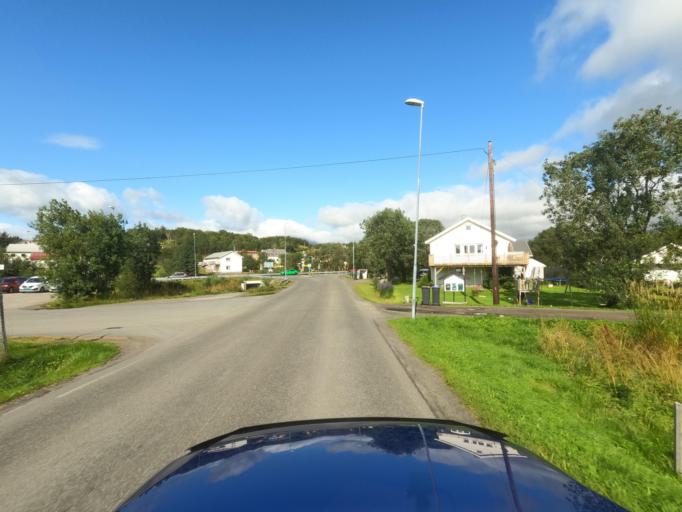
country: NO
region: Nordland
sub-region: Vestvagoy
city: Leknes
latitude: 68.1444
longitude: 13.6508
